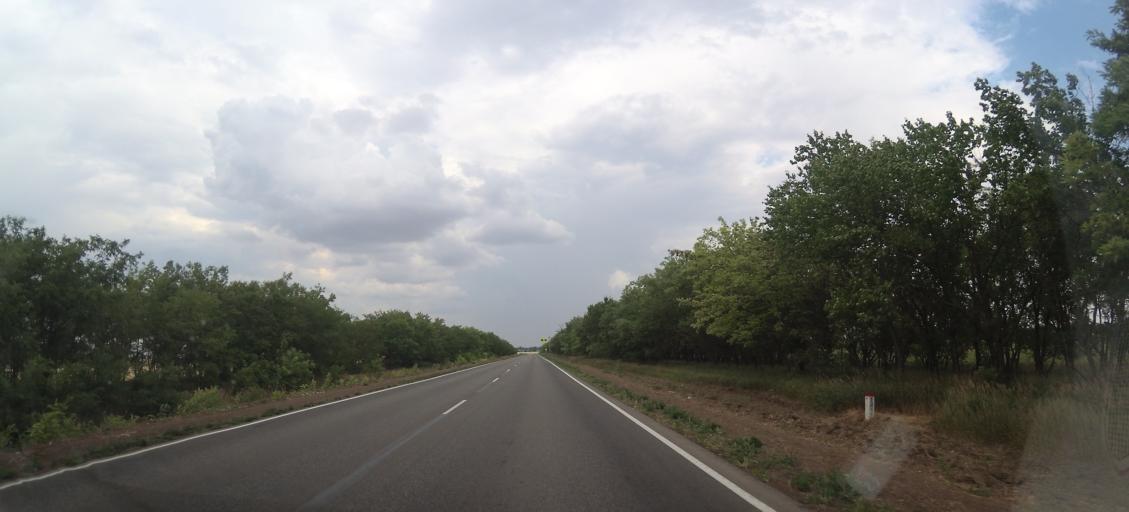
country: RU
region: Rostov
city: Gigant
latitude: 46.3420
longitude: 41.4132
